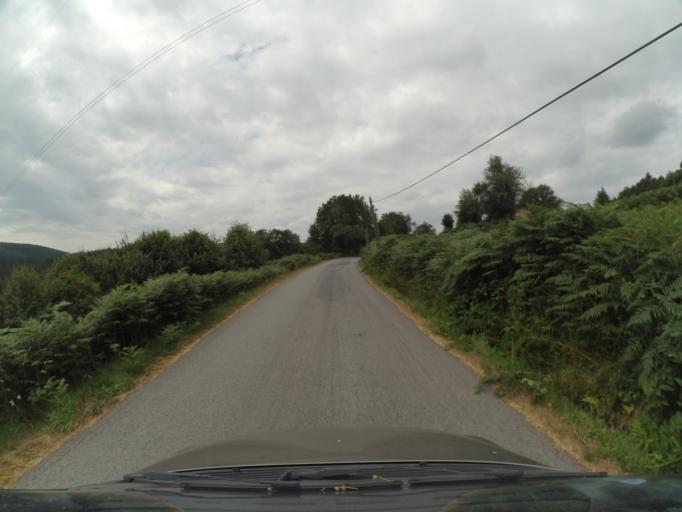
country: FR
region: Limousin
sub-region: Departement de la Creuse
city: La Courtine
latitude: 45.6661
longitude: 2.1476
